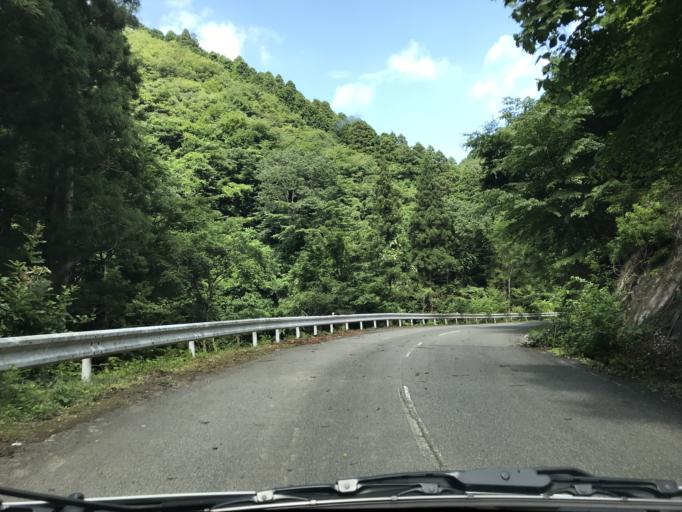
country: JP
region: Iwate
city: Tono
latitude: 39.0743
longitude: 141.4074
